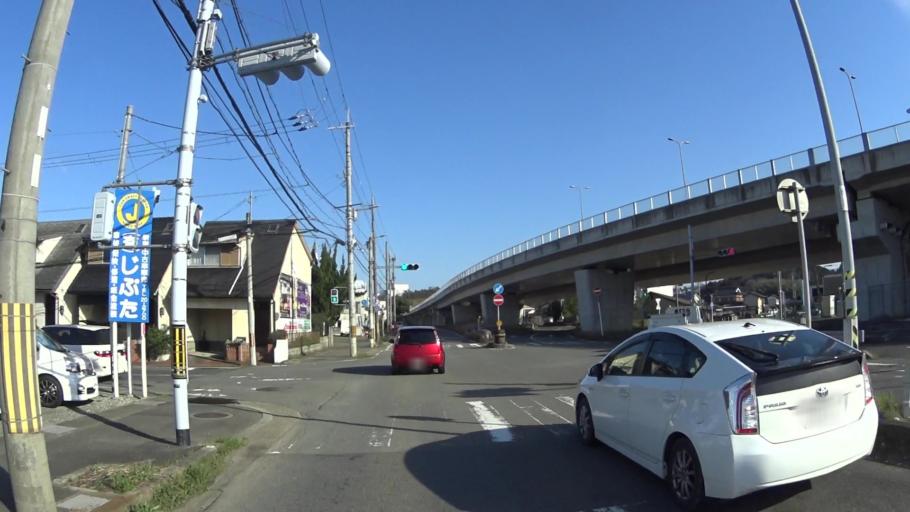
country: JP
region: Kyoto
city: Fukuchiyama
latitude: 35.2911
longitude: 135.1451
